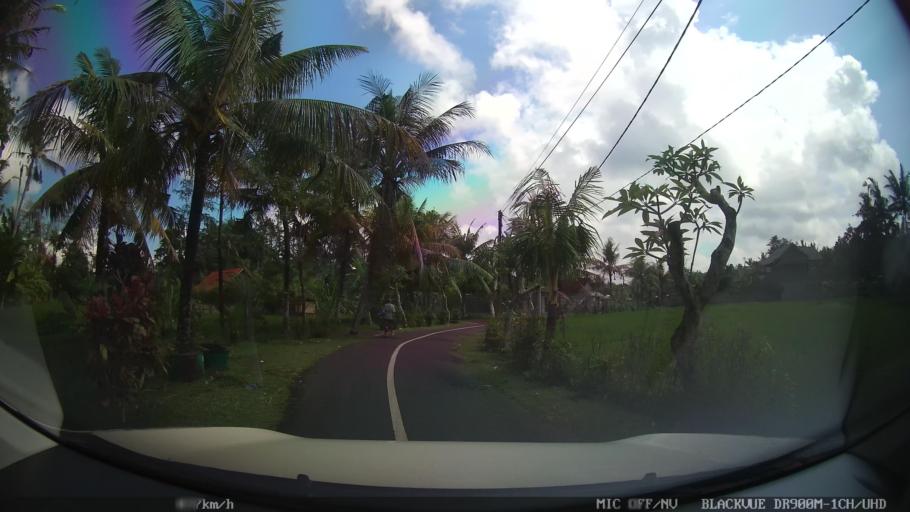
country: ID
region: Bali
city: Banjar Tebongkang
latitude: -8.5490
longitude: 115.2752
